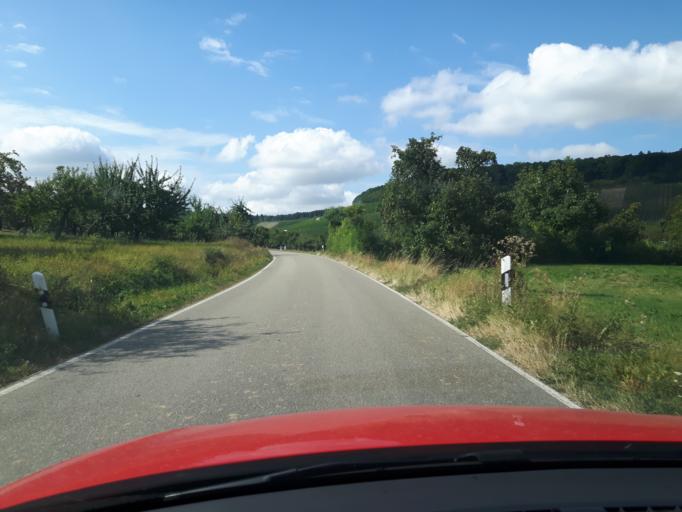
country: DE
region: Baden-Wuerttemberg
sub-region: Regierungsbezirk Stuttgart
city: Nordheim
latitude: 49.1192
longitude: 9.1075
